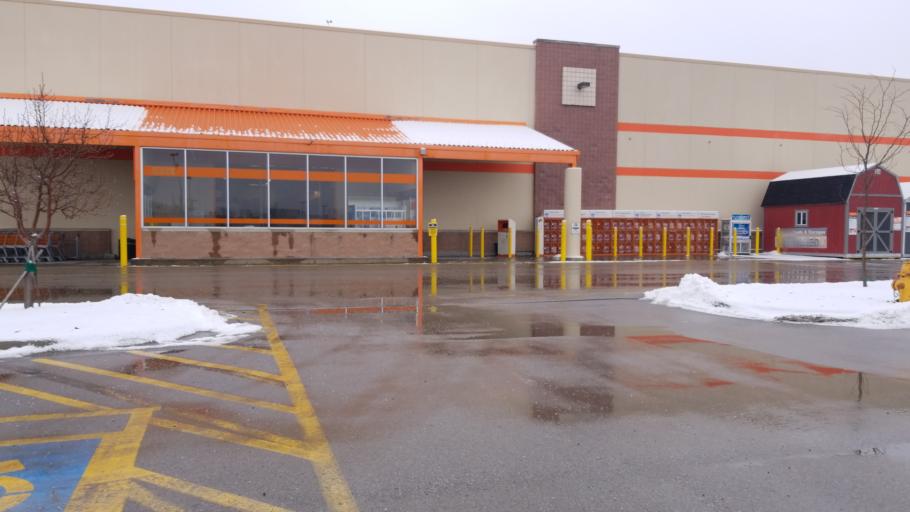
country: US
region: Iowa
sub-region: Pottawattamie County
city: Council Bluffs
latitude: 41.2301
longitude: -95.8460
